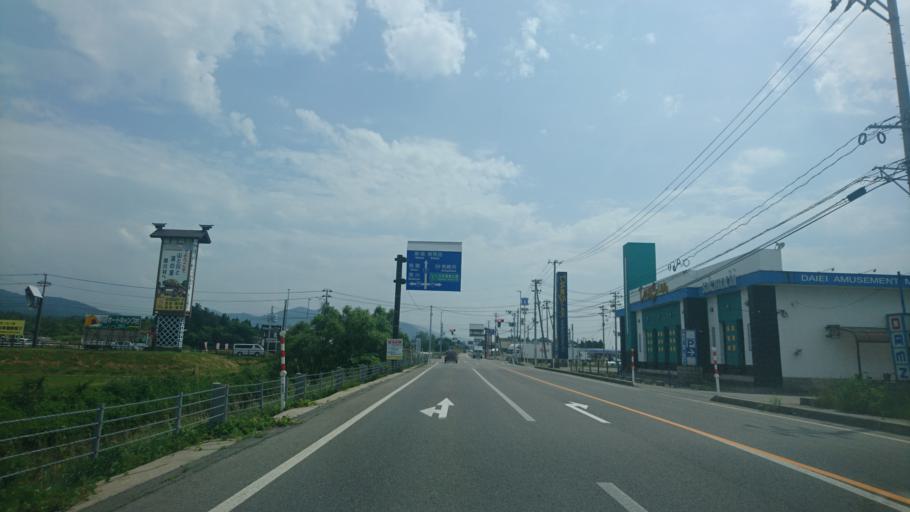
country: JP
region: Niigata
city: Murakami
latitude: 38.1071
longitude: 139.4472
